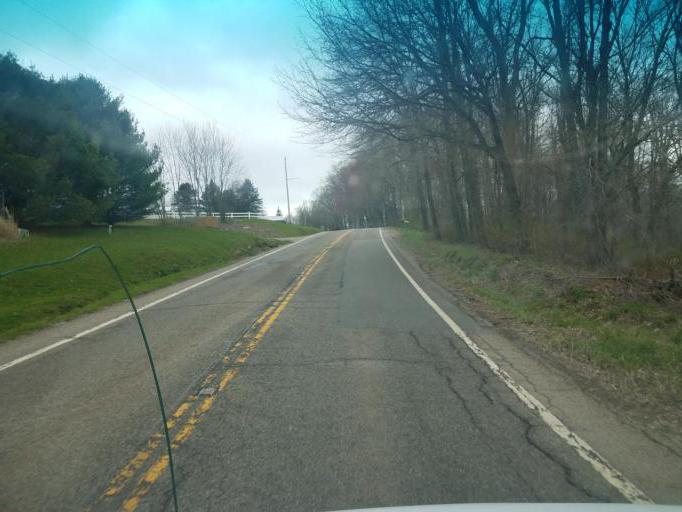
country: US
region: Ohio
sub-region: Stark County
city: Beach City
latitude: 40.5989
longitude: -81.6031
